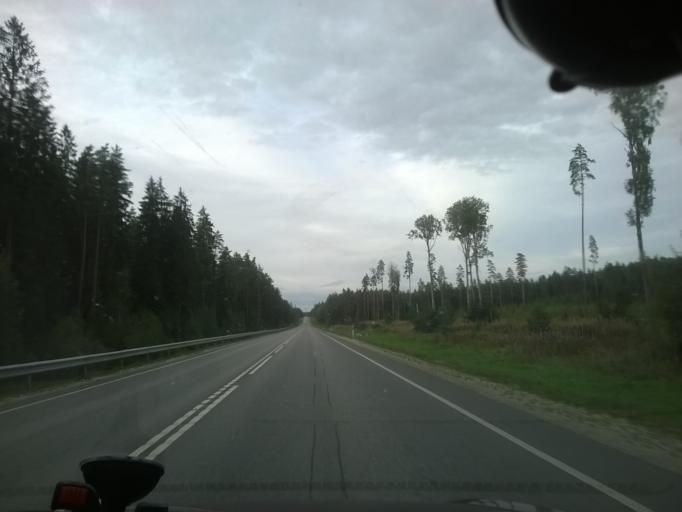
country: EE
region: Vorumaa
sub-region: Voru linn
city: Voru
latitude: 57.9379
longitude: 26.7973
